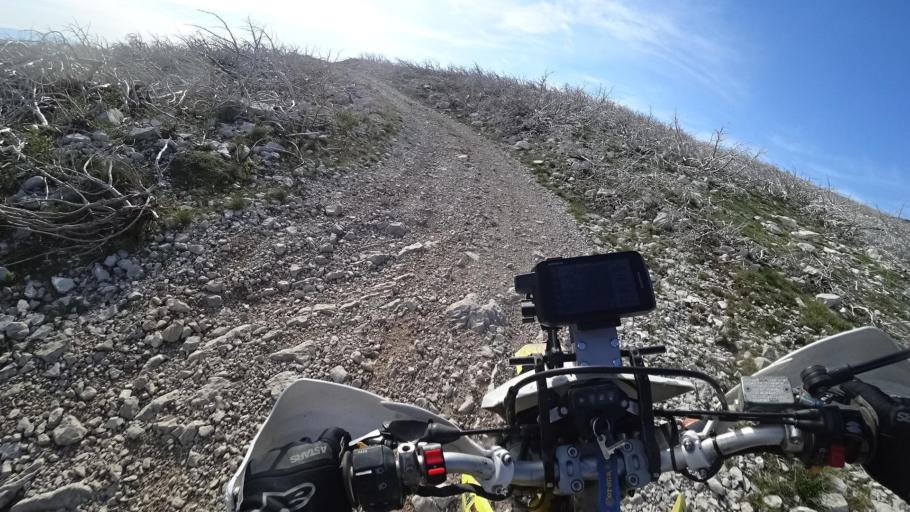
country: BA
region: Federation of Bosnia and Herzegovina
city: Kocerin
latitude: 43.5882
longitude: 17.5381
